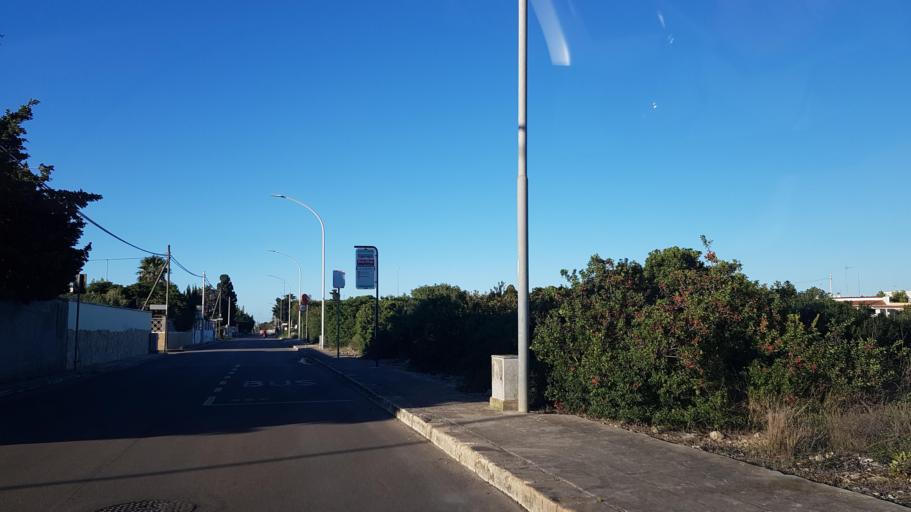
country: IT
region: Apulia
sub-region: Provincia di Lecce
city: Giorgilorio
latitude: 40.4605
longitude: 18.1951
